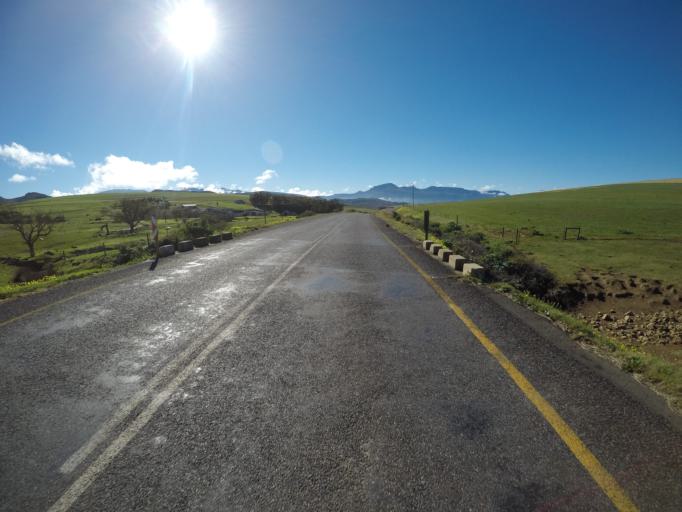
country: ZA
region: Western Cape
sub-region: Overberg District Municipality
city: Caledon
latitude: -34.1251
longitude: 19.5145
